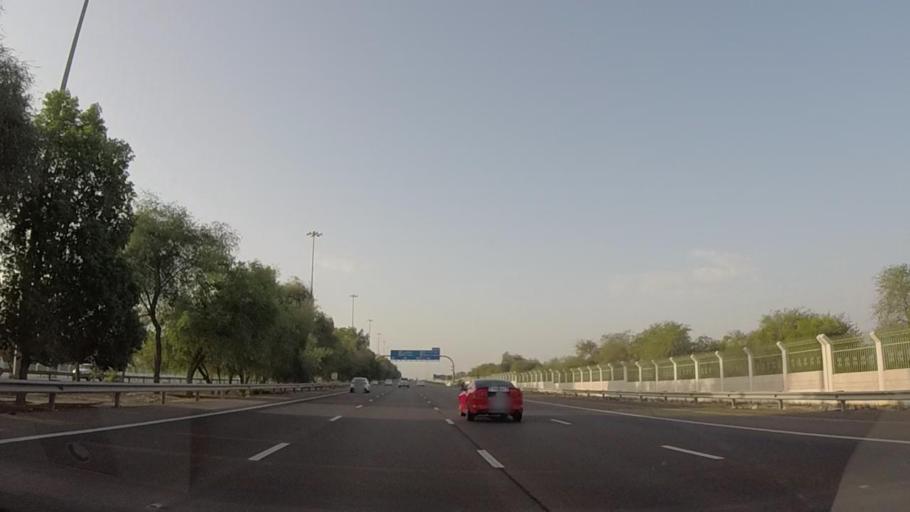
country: AE
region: Dubai
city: Dubai
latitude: 24.8073
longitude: 54.8675
